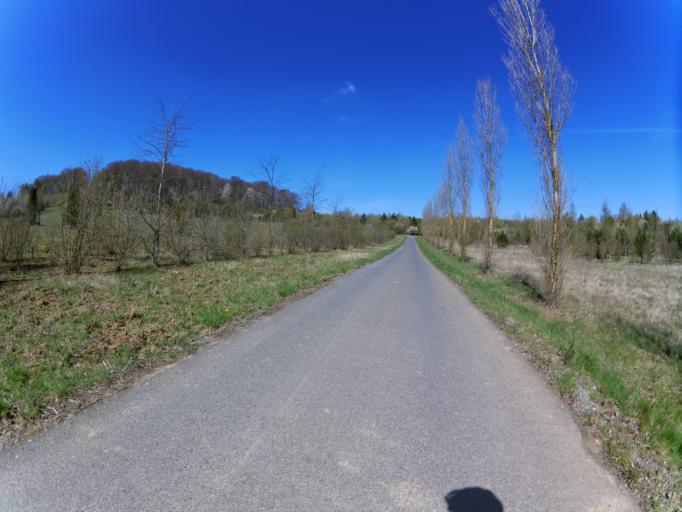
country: DE
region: Bavaria
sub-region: Regierungsbezirk Unterfranken
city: Hettstadt
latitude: 49.8145
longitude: 9.7945
